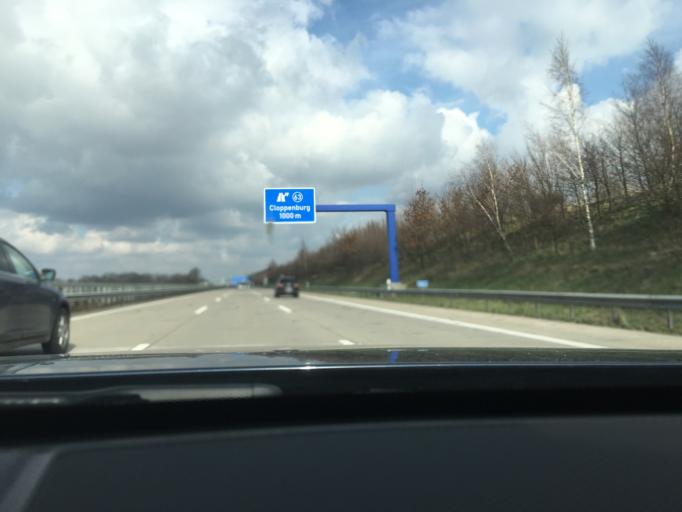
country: DE
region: Lower Saxony
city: Buehren
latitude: 52.8009
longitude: 8.2069
